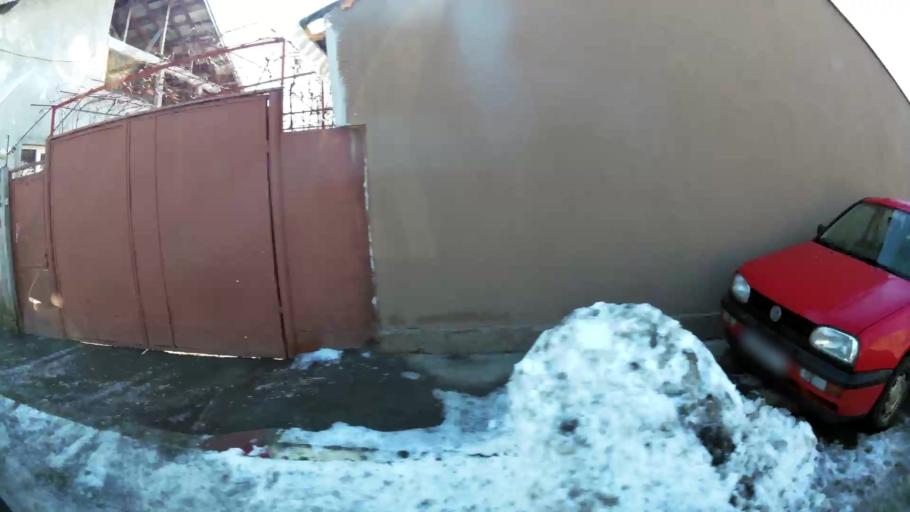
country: RO
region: Ilfov
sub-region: Comuna Magurele
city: Magurele
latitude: 44.3828
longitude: 26.0516
